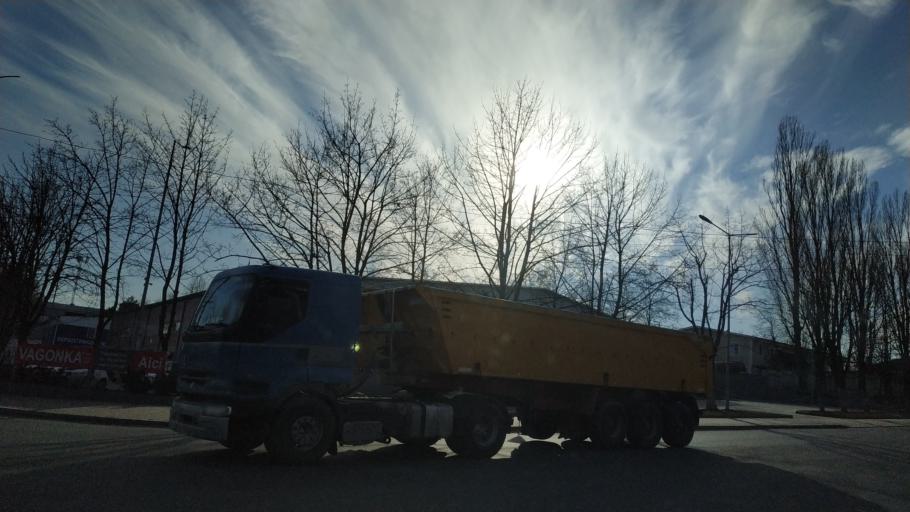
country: MD
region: Chisinau
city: Chisinau
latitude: 47.0269
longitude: 28.8957
